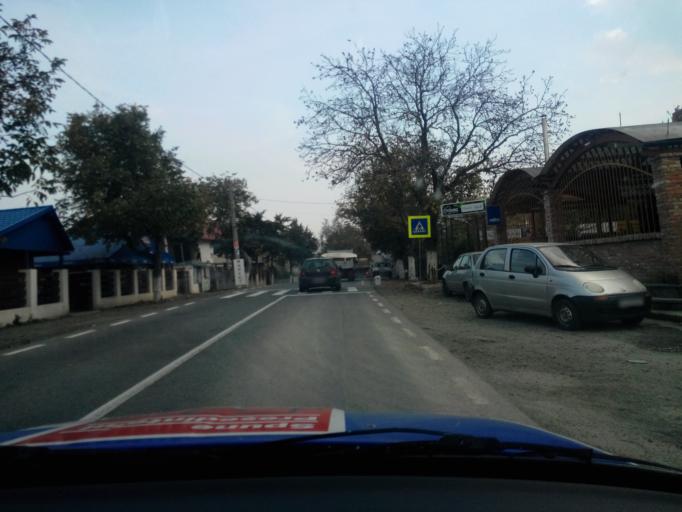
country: RO
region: Tulcea
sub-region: Comuna Somova
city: Somova
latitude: 45.1874
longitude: 28.6636
